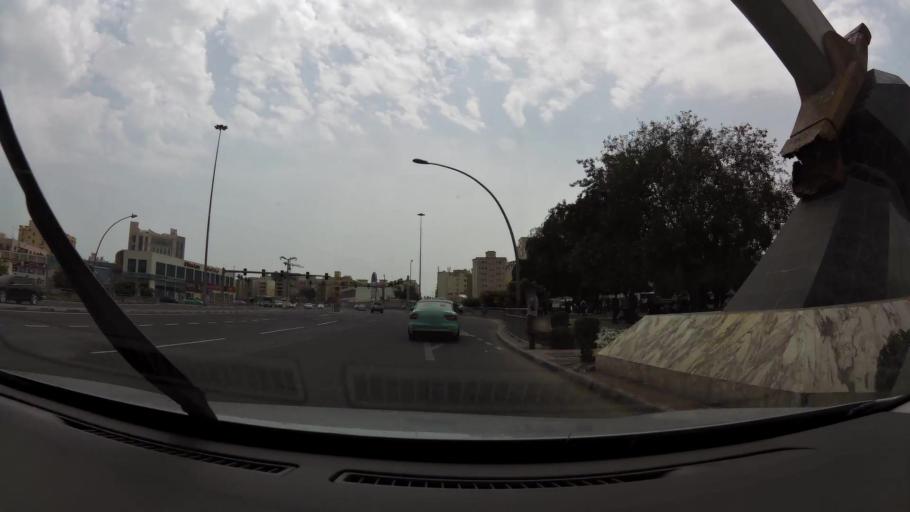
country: QA
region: Baladiyat ad Dawhah
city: Doha
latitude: 25.2808
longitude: 51.5349
